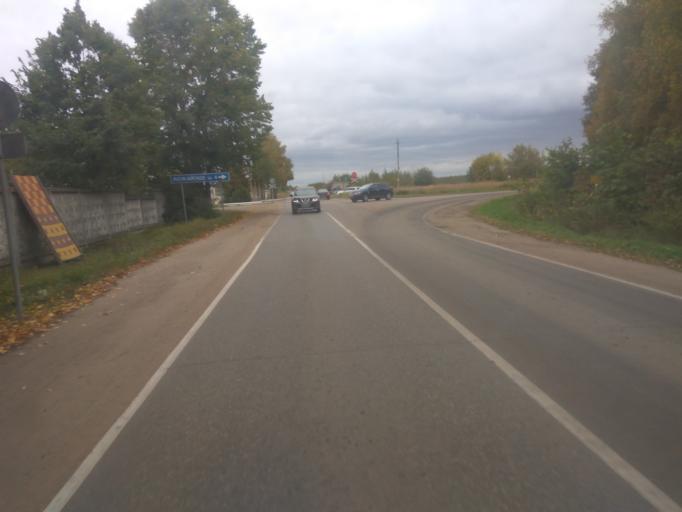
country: RU
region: Moskovskaya
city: Chupryakovo
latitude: 55.6046
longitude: 36.6222
